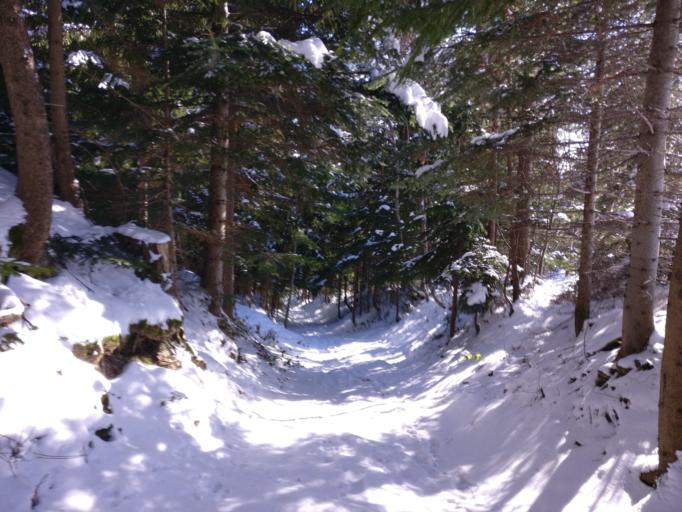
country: AT
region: Styria
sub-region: Politischer Bezirk Hartberg-Fuerstenfeld
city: Sankt Jakob im Walde
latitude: 47.4729
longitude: 15.7871
